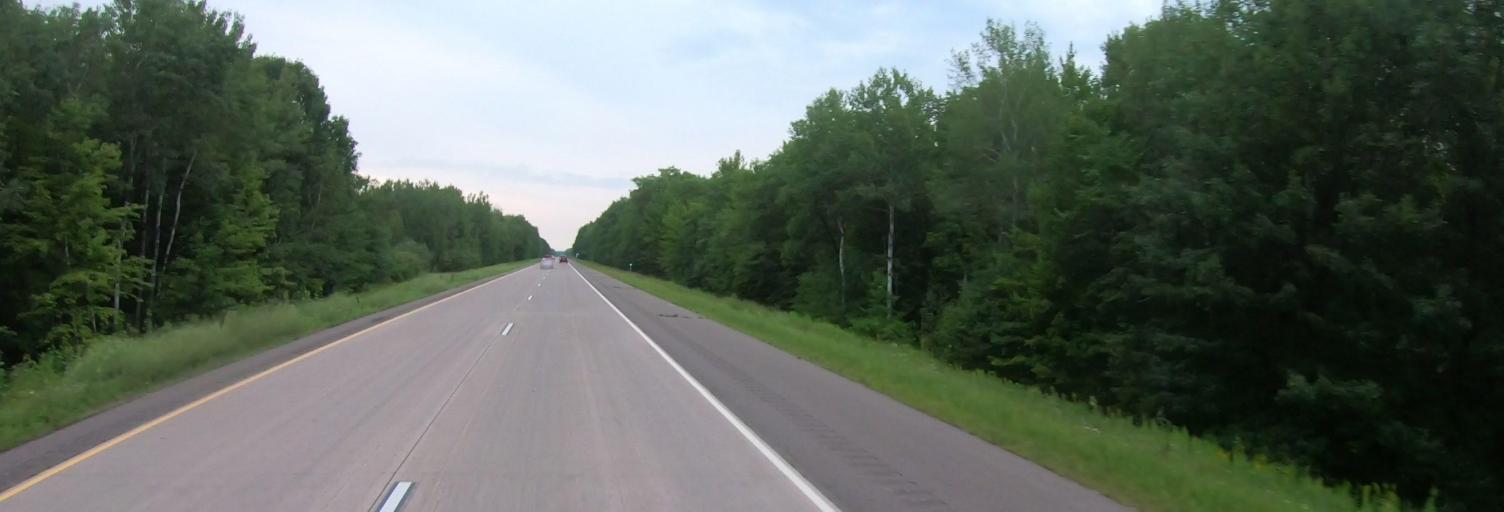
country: US
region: Minnesota
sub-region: Pine County
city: Sandstone
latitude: 46.0749
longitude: -92.9016
